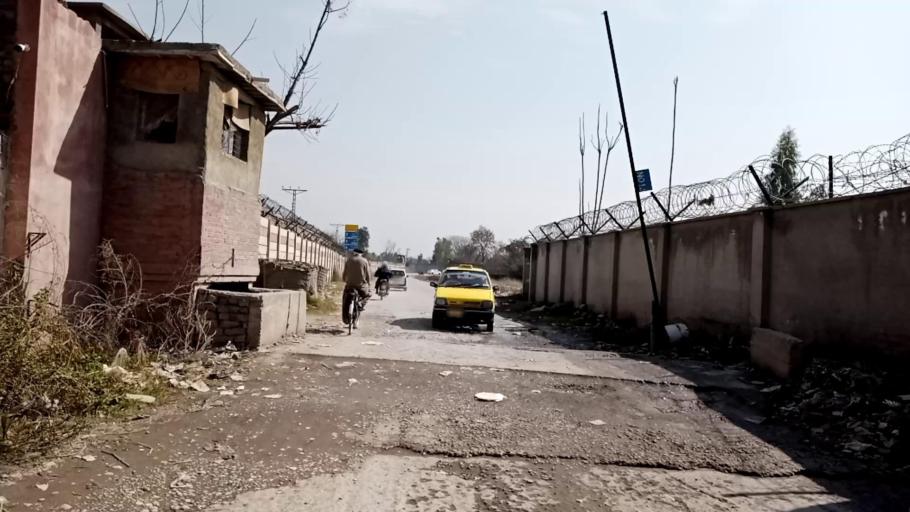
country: PK
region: Khyber Pakhtunkhwa
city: Peshawar
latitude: 33.9945
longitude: 71.5084
